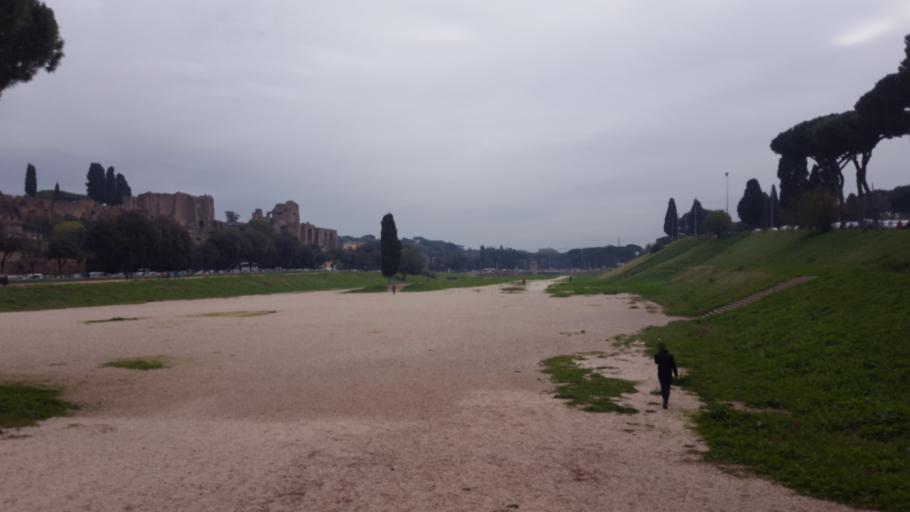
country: IT
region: Latium
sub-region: Citta metropolitana di Roma Capitale
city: Rome
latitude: 41.8873
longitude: 12.4828
